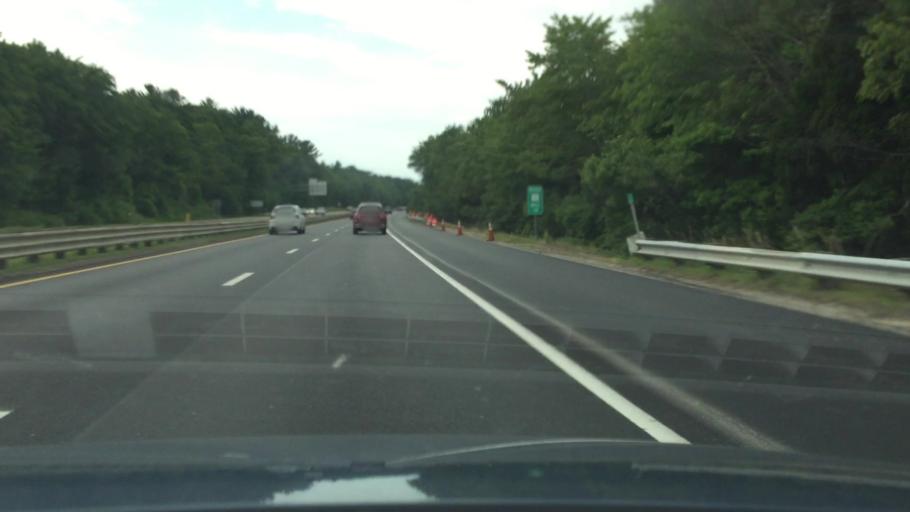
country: US
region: Massachusetts
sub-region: Plymouth County
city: Kingston
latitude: 42.0047
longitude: -70.7246
